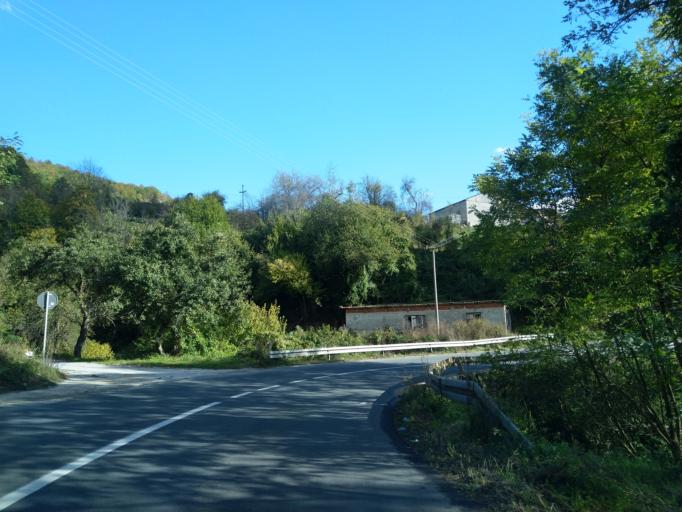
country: RS
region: Central Serbia
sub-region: Zlatiborski Okrug
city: Uzice
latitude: 43.8753
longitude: 19.7932
